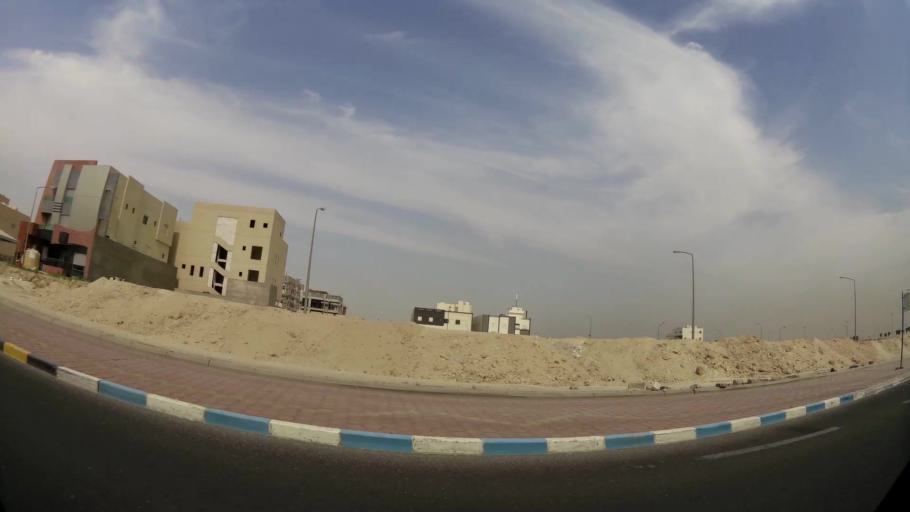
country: KW
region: Al Farwaniyah
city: Janub as Surrah
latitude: 29.2864
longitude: 48.0007
